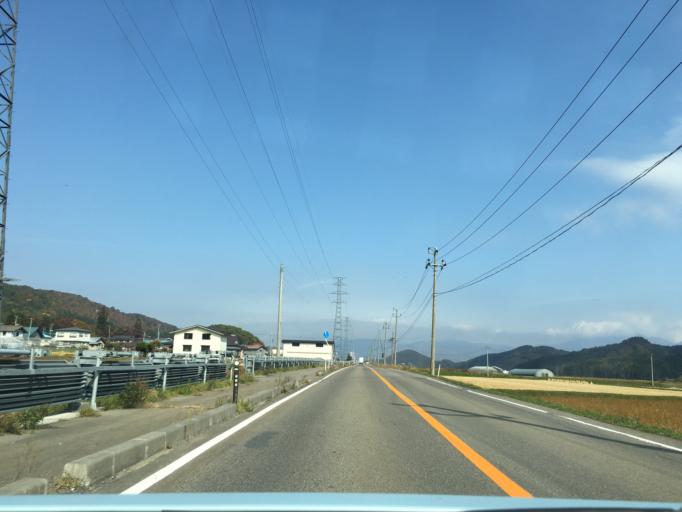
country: JP
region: Fukushima
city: Inawashiro
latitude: 37.4623
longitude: 140.0129
